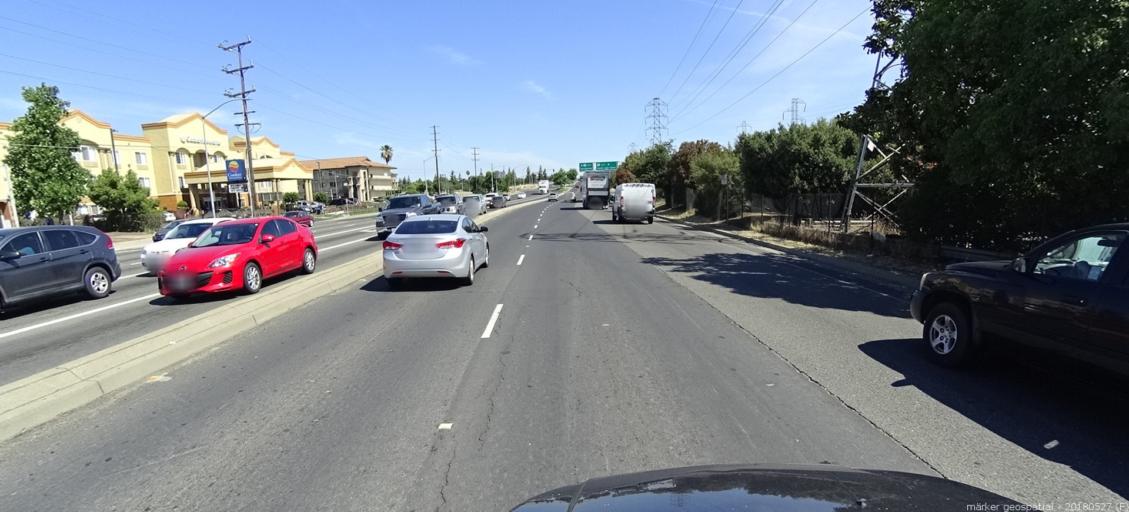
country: US
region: California
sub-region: Sacramento County
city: Rosemont
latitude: 38.5500
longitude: -121.4091
